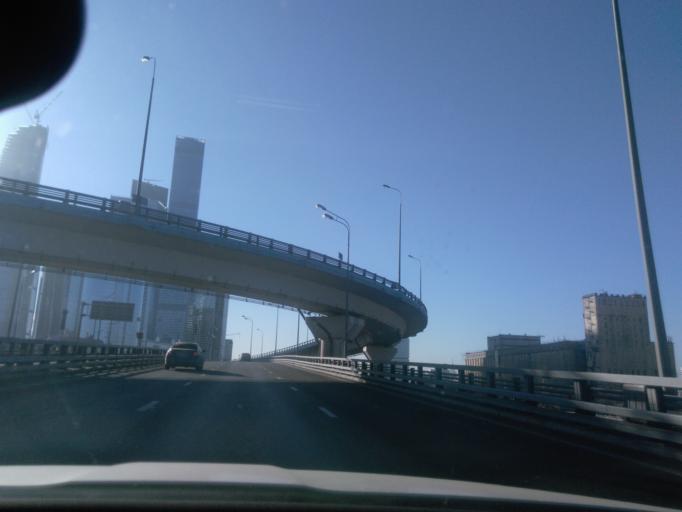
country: RU
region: Moskovskaya
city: Presnenskiy
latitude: 55.7558
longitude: 37.5277
